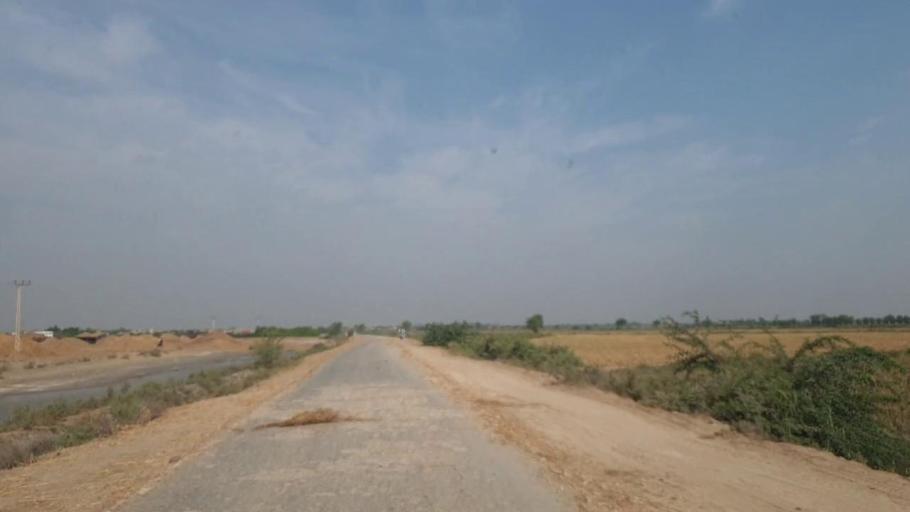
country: PK
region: Sindh
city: Tando Bago
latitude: 24.9062
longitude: 68.9966
